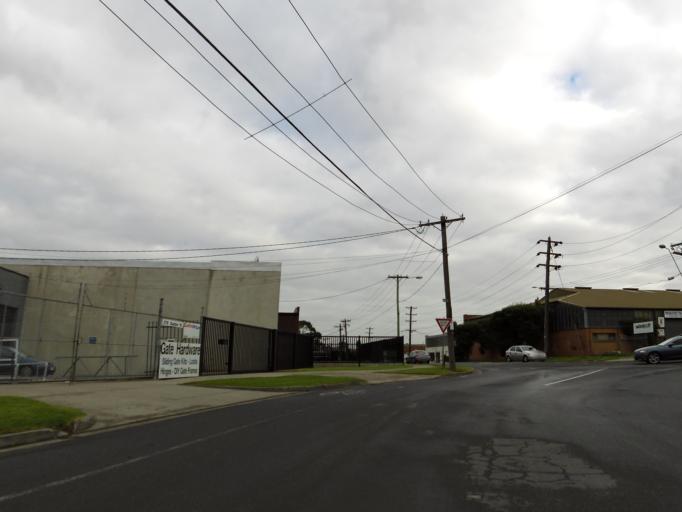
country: AU
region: Victoria
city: Heidelberg West
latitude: -37.7555
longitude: 145.0289
